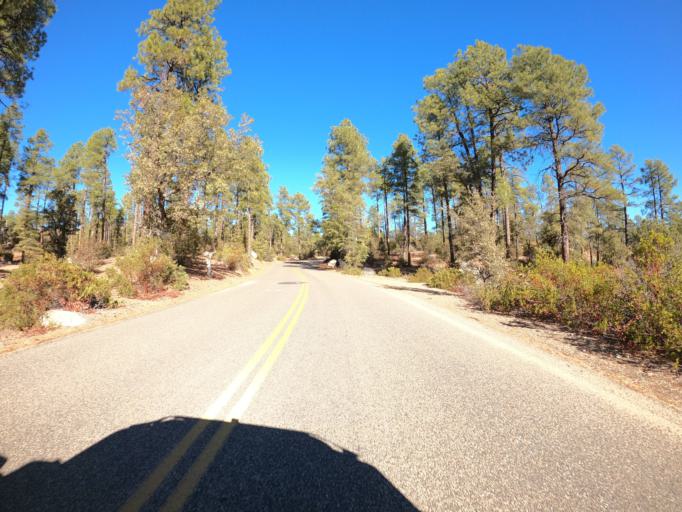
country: US
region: Arizona
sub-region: Yavapai County
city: Verde Village
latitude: 34.5792
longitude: -112.0635
